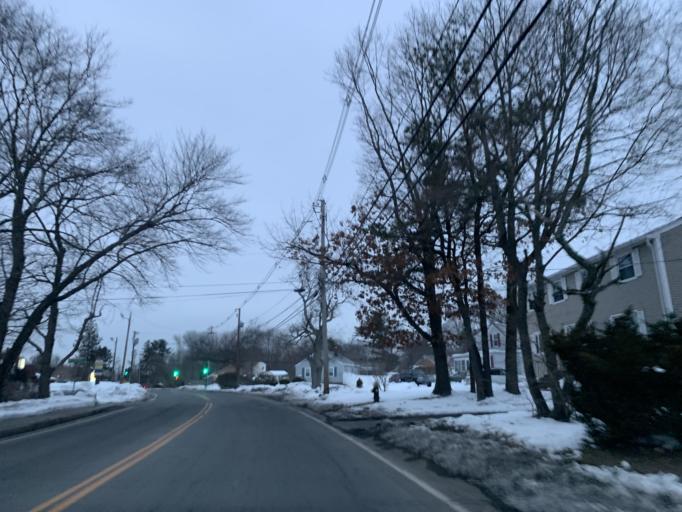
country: US
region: Massachusetts
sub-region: Norfolk County
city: Stoughton
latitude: 42.1356
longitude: -71.1112
